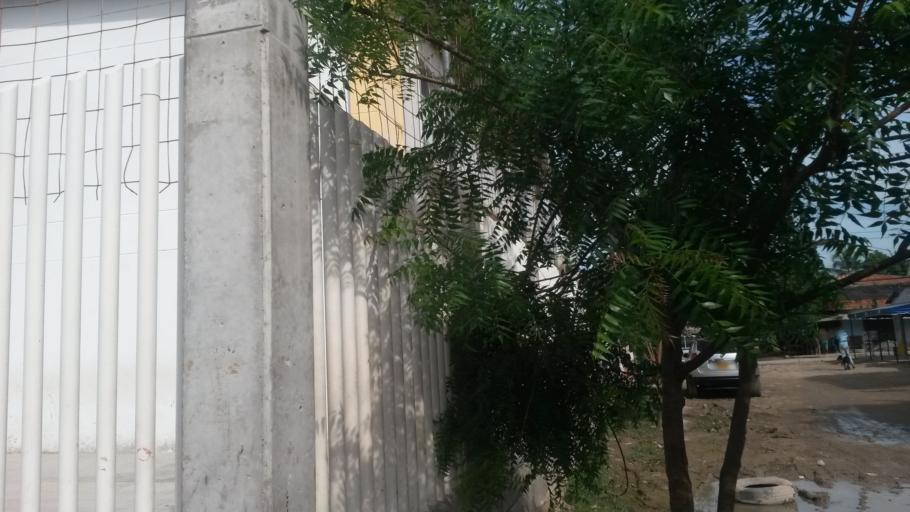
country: CO
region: Bolivar
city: Cartagena
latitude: 10.4070
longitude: -75.4529
